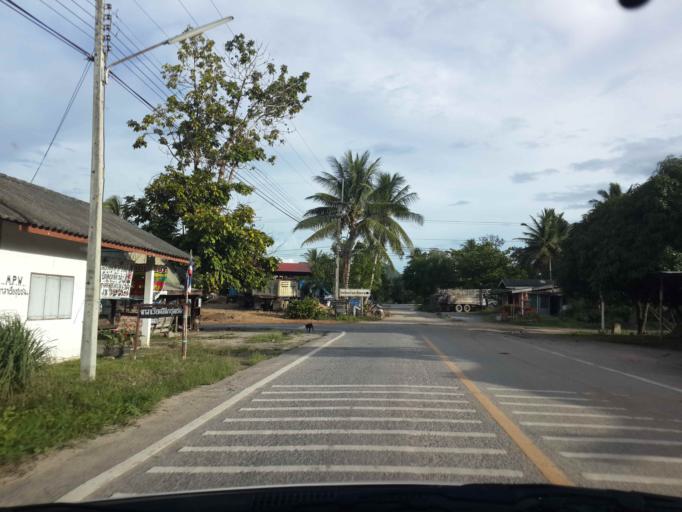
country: TH
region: Kanchanaburi
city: Dan Makham Tia
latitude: 13.8166
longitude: 99.1717
